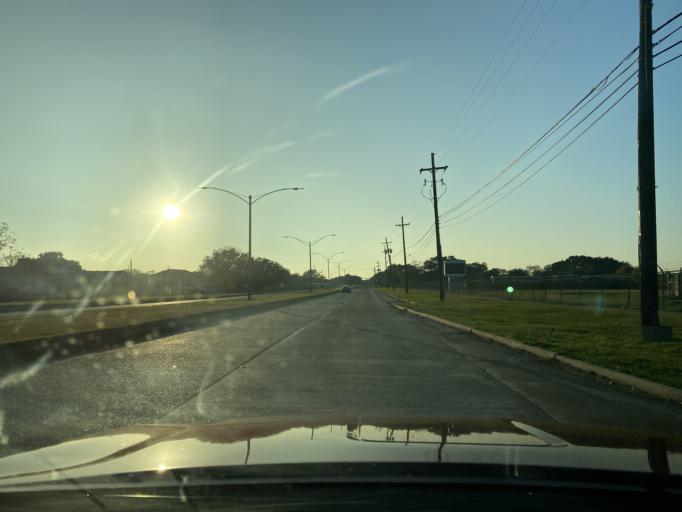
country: US
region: Louisiana
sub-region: Orleans Parish
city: New Orleans
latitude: 30.0270
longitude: -90.0486
